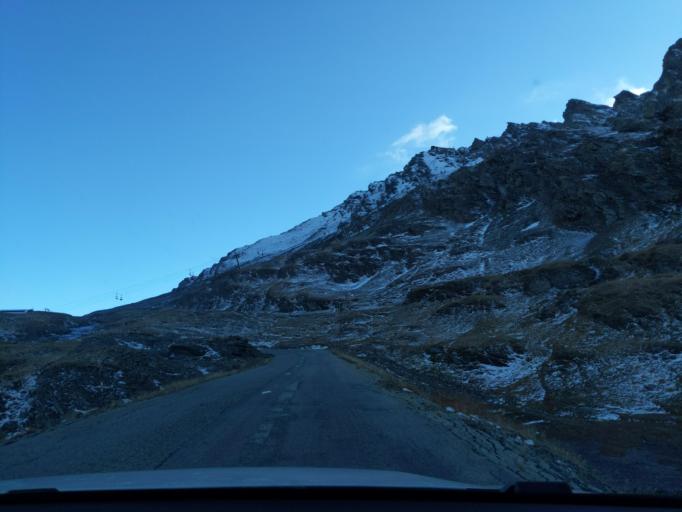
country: FR
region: Rhone-Alpes
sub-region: Departement de la Savoie
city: Val-d'Isere
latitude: 45.4248
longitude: 7.0227
